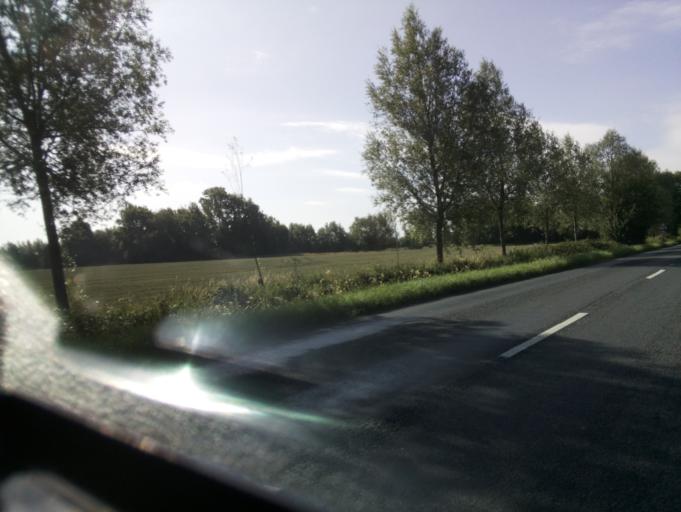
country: GB
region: England
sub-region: Oxfordshire
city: Faringdon
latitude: 51.7007
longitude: -1.5910
